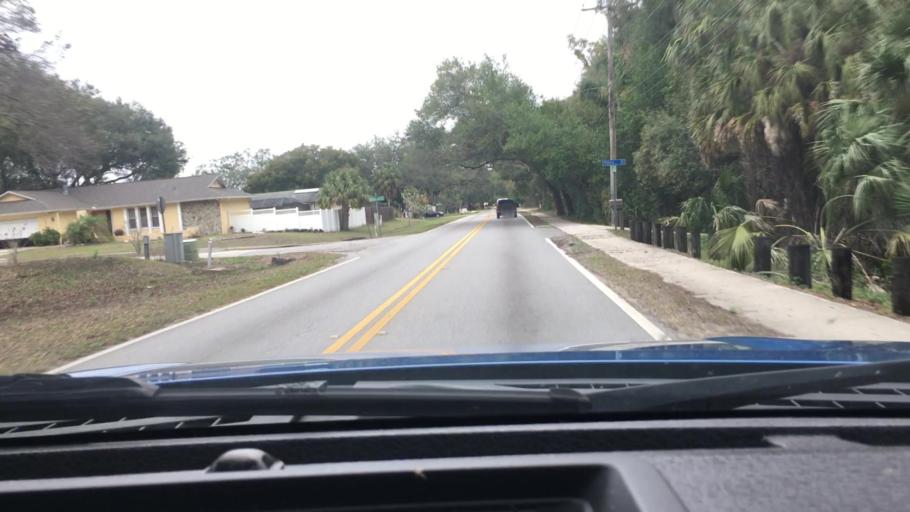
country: US
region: Florida
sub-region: Hillsborough County
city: Mango
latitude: 27.9616
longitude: -82.3104
